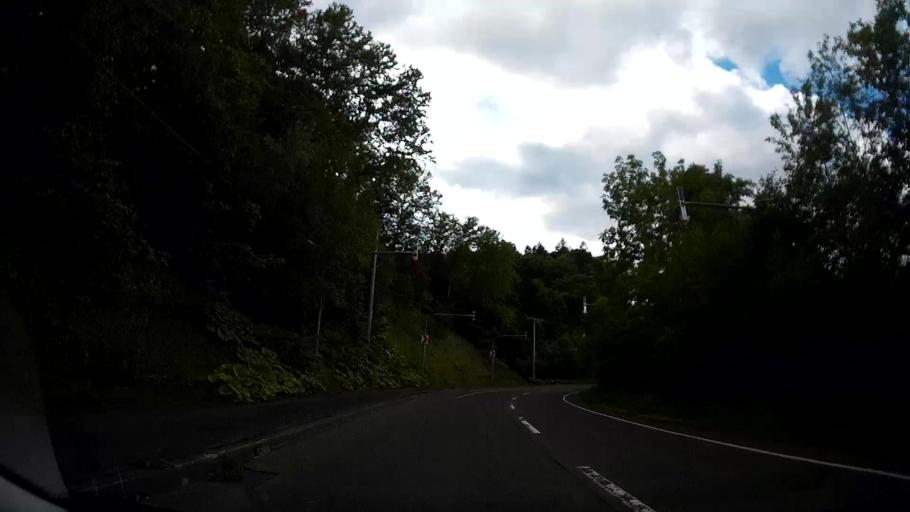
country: JP
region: Hokkaido
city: Kitahiroshima
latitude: 42.8433
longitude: 141.4481
